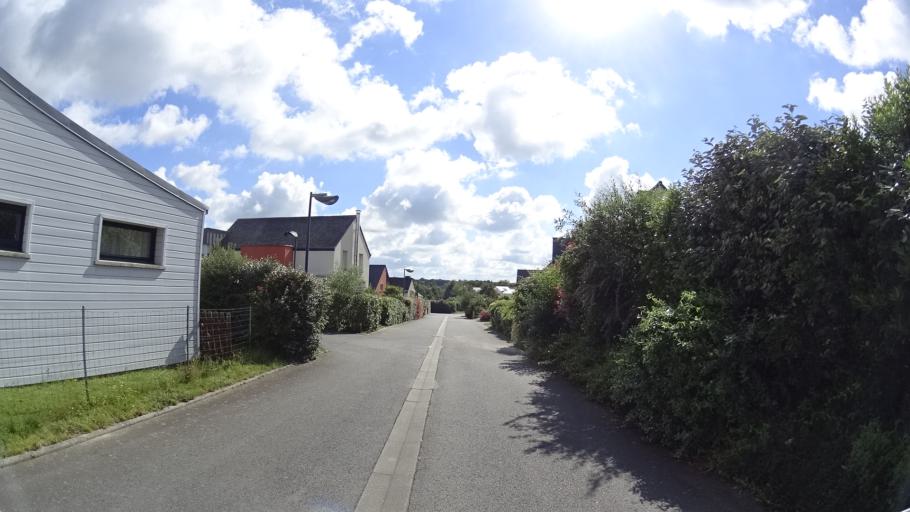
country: FR
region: Brittany
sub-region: Departement d'Ille-et-Vilaine
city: Le Rheu
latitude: 48.1293
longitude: -1.8073
